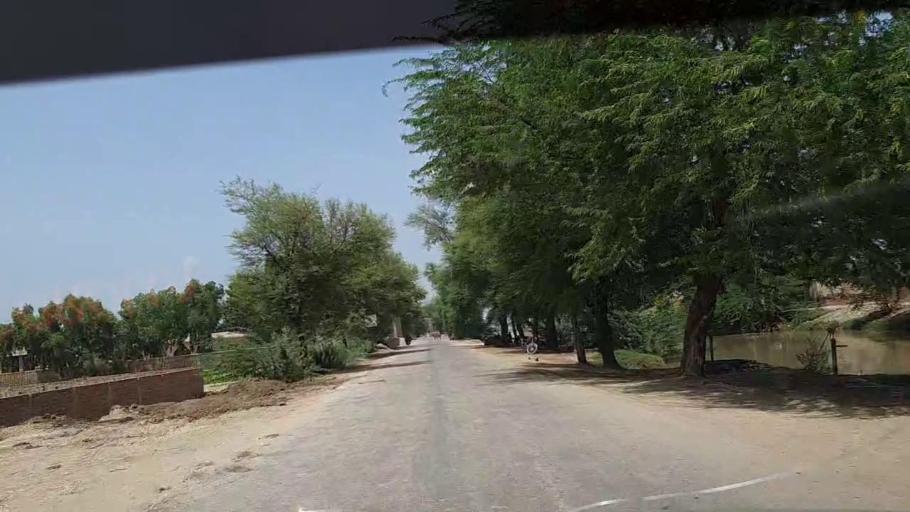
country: PK
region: Sindh
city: Khanpur
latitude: 27.8391
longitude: 69.4086
